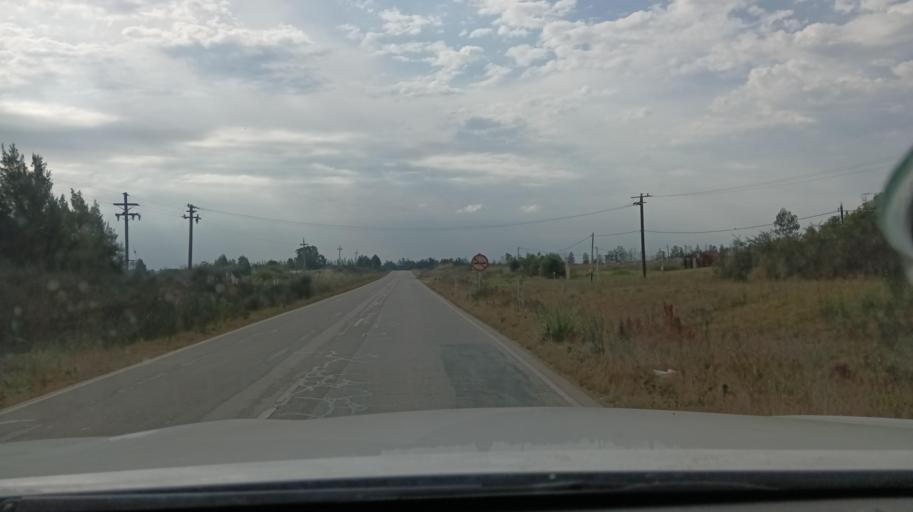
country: UY
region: Canelones
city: Sauce
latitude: -34.6578
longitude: -56.1084
